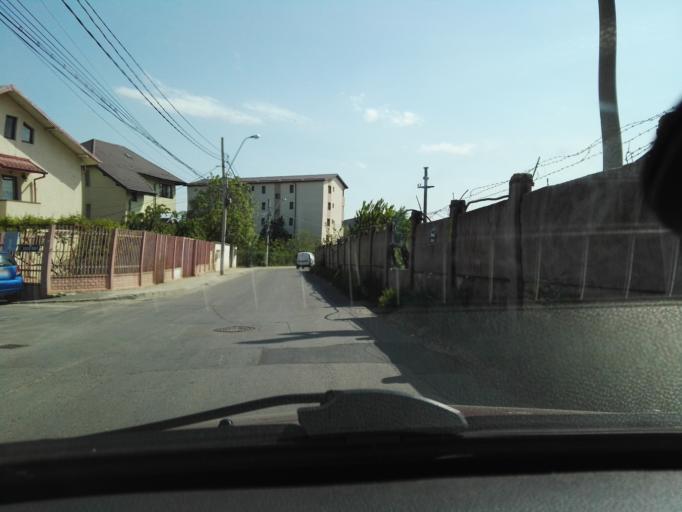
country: RO
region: Ilfov
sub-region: Comuna Popesti-Leordeni
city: Popesti-Leordeni
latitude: 44.3726
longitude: 26.1290
